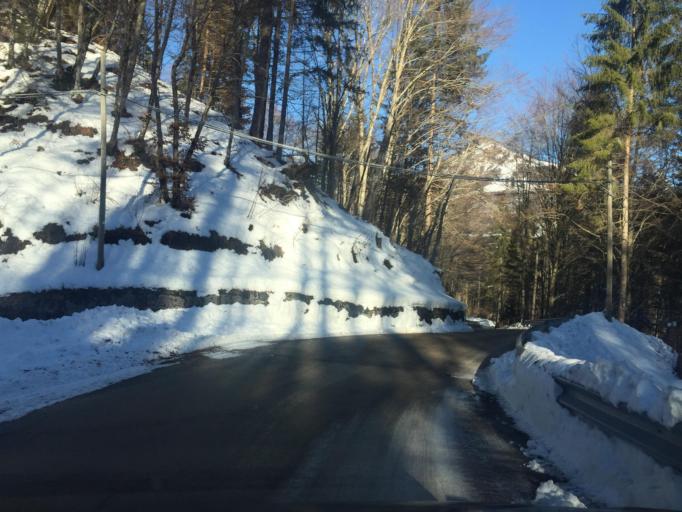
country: IT
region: Friuli Venezia Giulia
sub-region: Provincia di Udine
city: Lauco
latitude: 46.4327
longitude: 12.9483
